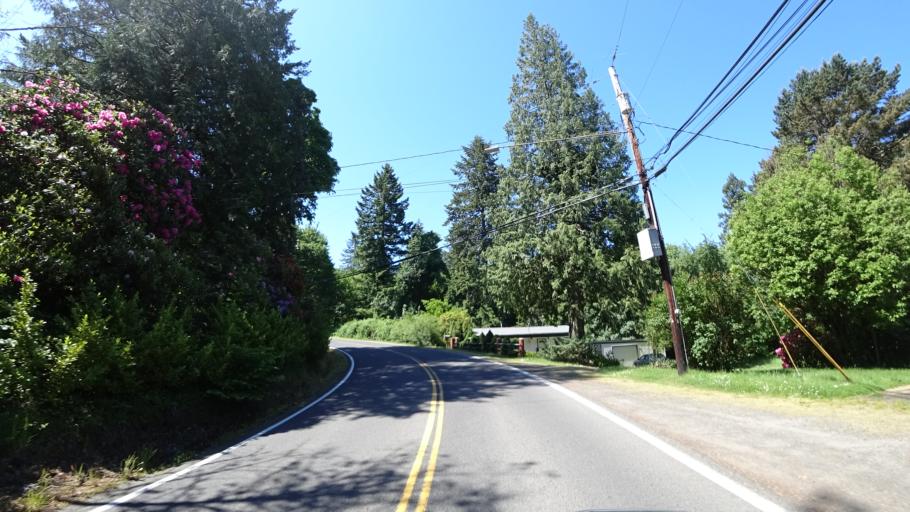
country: US
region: Oregon
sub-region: Clackamas County
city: Happy Valley
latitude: 45.4678
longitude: -122.5245
